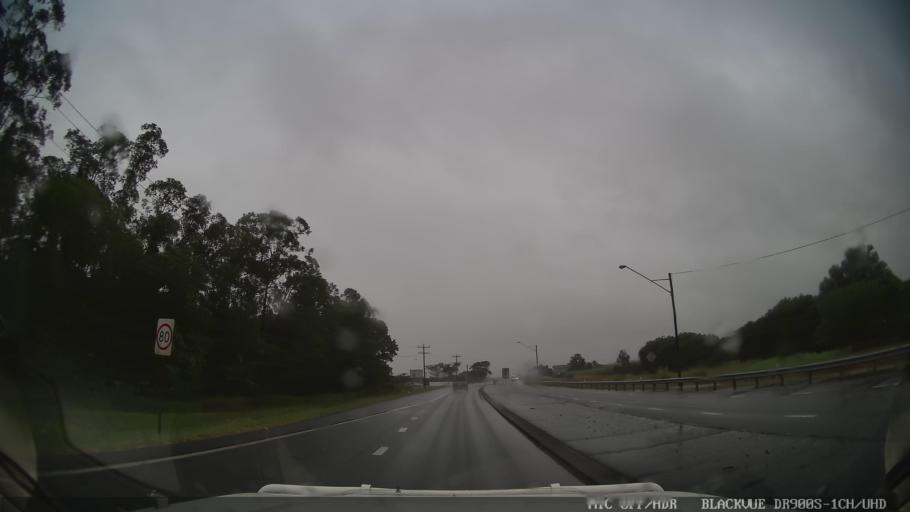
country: AU
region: Queensland
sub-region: Cassowary Coast
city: Innisfail
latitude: -17.7471
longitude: 146.0281
